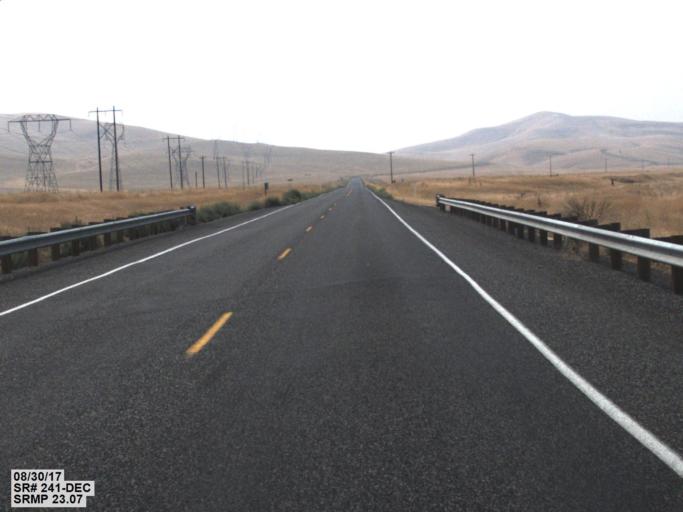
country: US
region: Washington
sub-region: Grant County
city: Desert Aire
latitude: 46.5067
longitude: -119.8816
